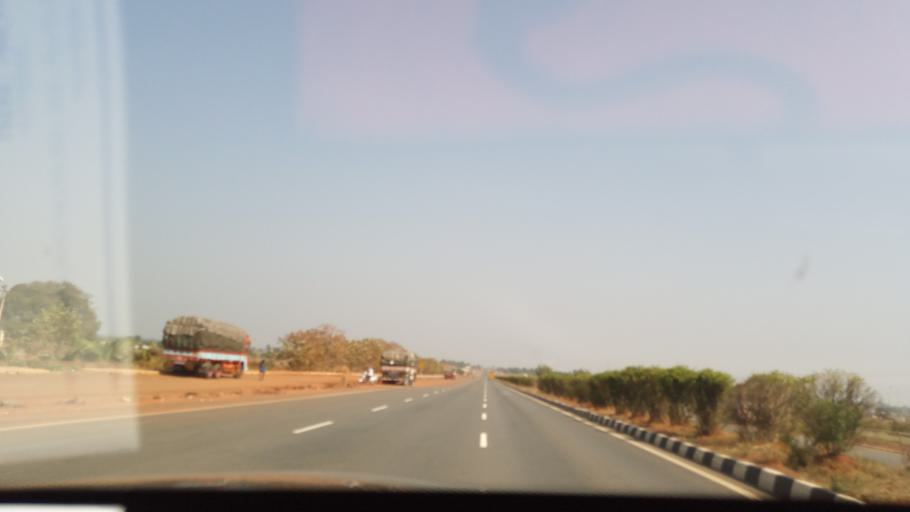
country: IN
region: Karnataka
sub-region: Haveri
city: Shiggaon
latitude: 15.0847
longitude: 75.1520
